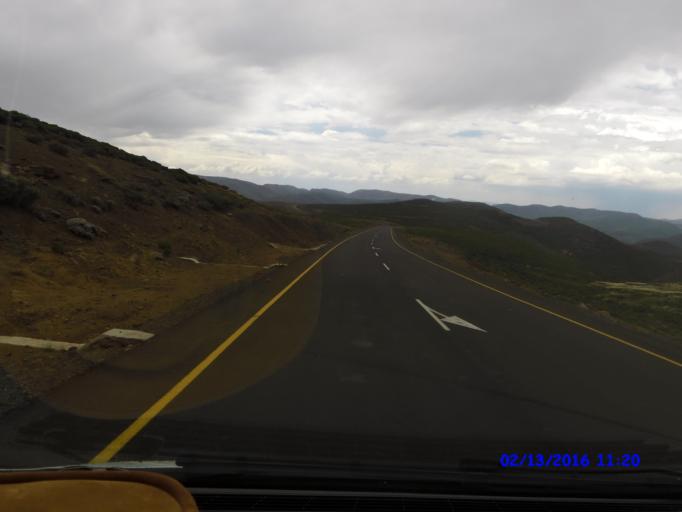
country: LS
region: Maseru
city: Nako
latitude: -29.7547
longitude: 27.9675
